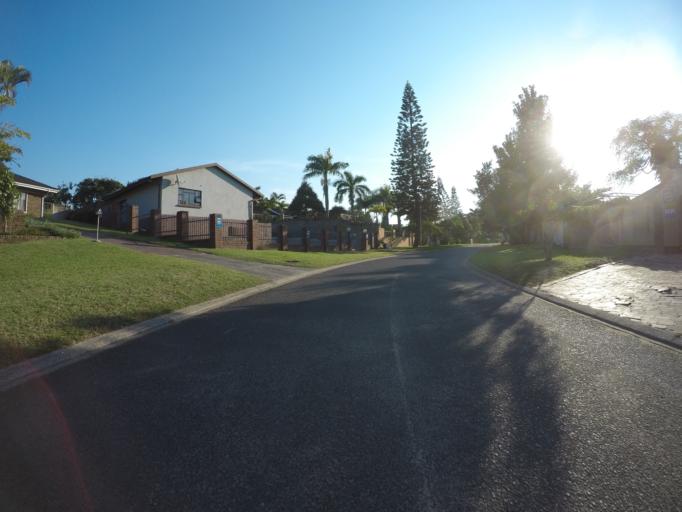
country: ZA
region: KwaZulu-Natal
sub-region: uThungulu District Municipality
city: Richards Bay
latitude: -28.7833
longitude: 32.1099
